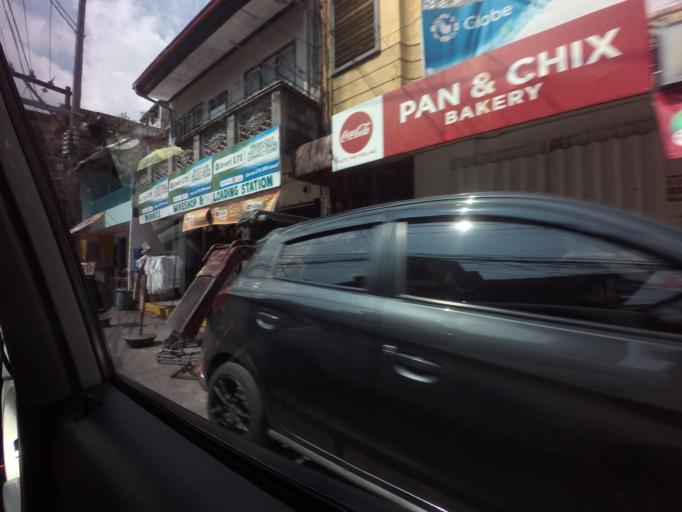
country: PH
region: Metro Manila
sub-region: City of Manila
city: Quiapo
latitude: 14.5998
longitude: 121.0018
